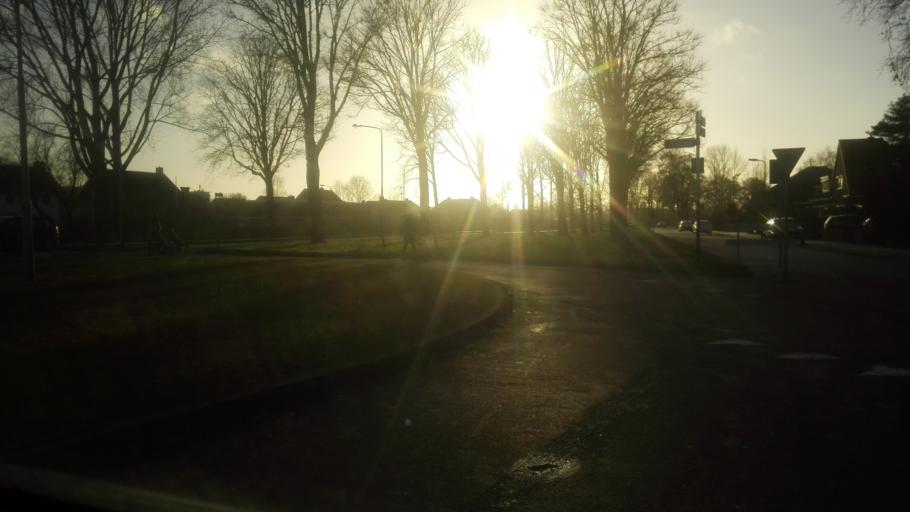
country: NL
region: Friesland
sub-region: Gemeente Heerenveen
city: Oranjewoud
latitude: 52.9504
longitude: 5.9348
